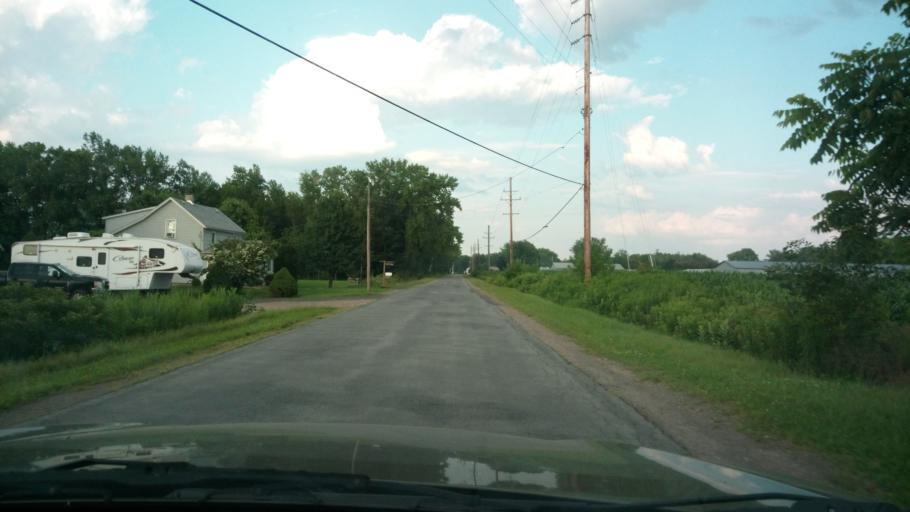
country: US
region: New York
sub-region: Wayne County
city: Clyde
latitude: 43.0888
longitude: -76.9016
